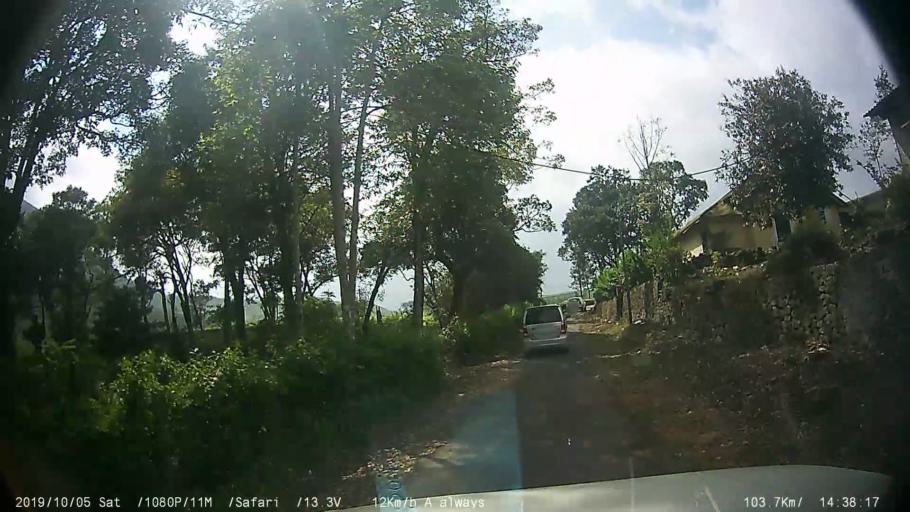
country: IN
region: Kerala
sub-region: Kottayam
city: Erattupetta
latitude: 9.6189
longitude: 76.9582
